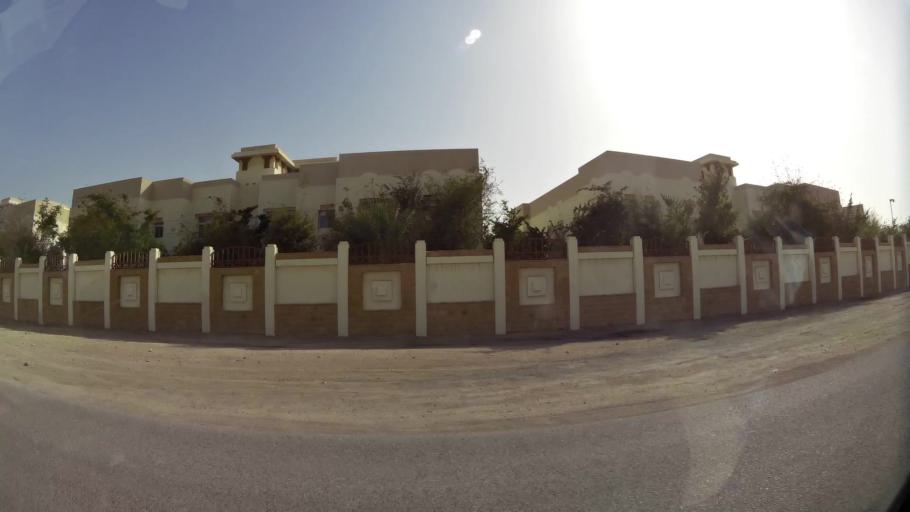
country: QA
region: Baladiyat ar Rayyan
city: Ar Rayyan
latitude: 25.3254
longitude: 51.4183
